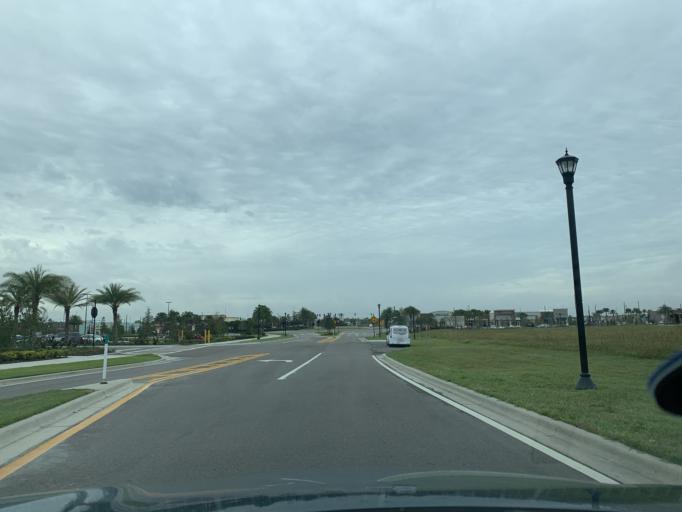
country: US
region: Florida
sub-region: Pasco County
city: Land O' Lakes
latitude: 28.1952
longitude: -82.3962
